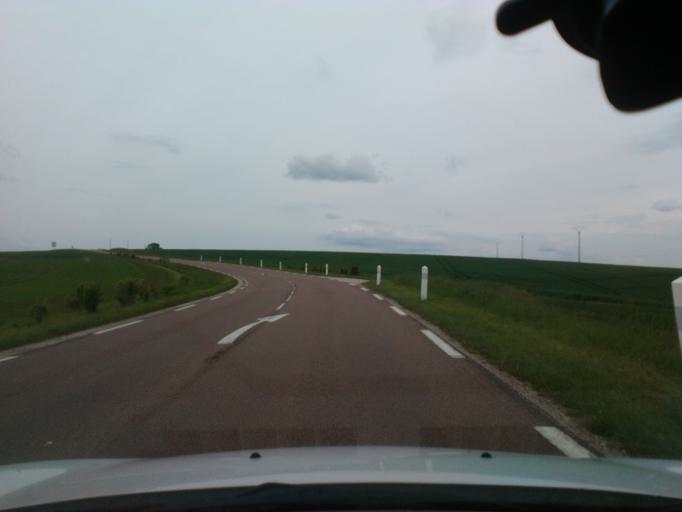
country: FR
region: Champagne-Ardenne
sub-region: Departement de l'Aube
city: Ville-sous-la-Ferte
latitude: 48.2173
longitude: 4.8208
